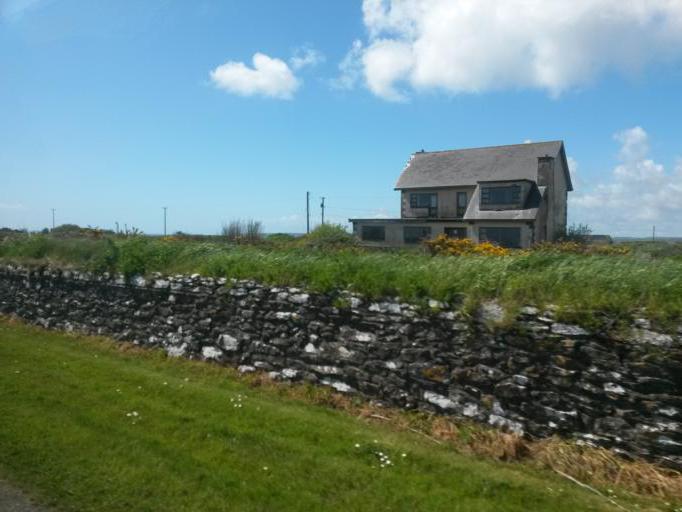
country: IE
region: Munster
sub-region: Waterford
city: Dunmore East
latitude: 52.1549
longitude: -6.8973
